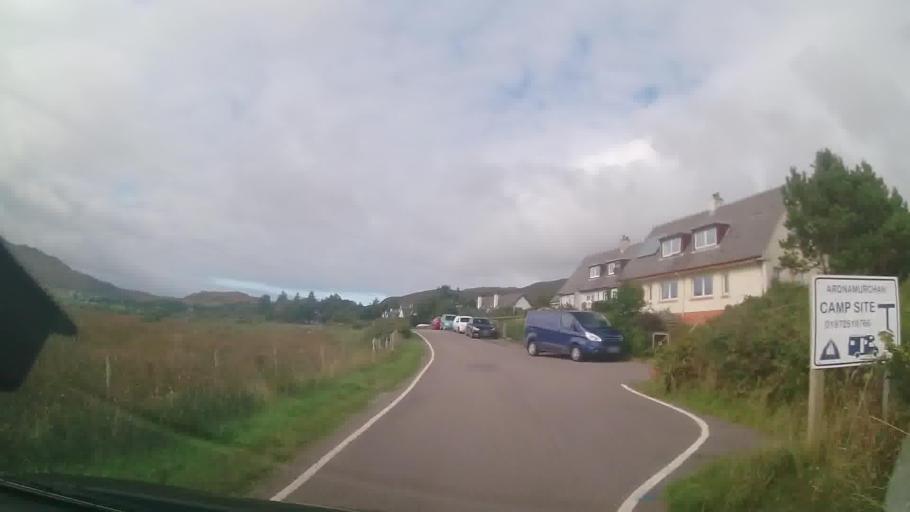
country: GB
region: Scotland
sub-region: Argyll and Bute
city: Isle Of Mull
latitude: 56.6928
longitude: -6.0949
